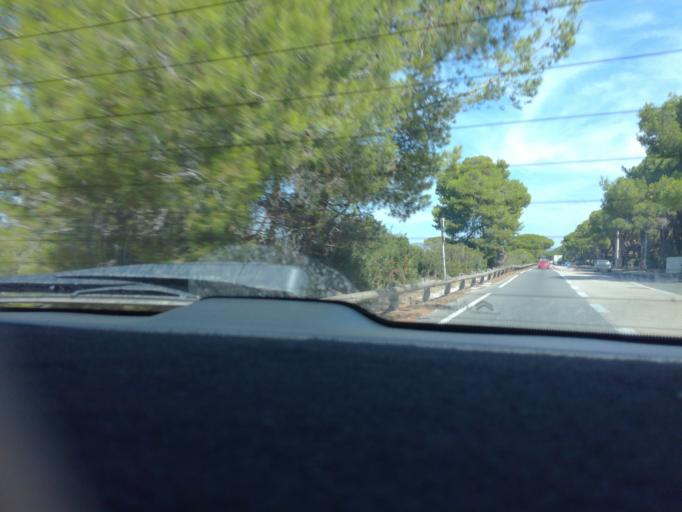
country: FR
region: Provence-Alpes-Cote d'Azur
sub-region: Departement du Var
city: Hyeres
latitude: 43.0752
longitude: 6.1488
